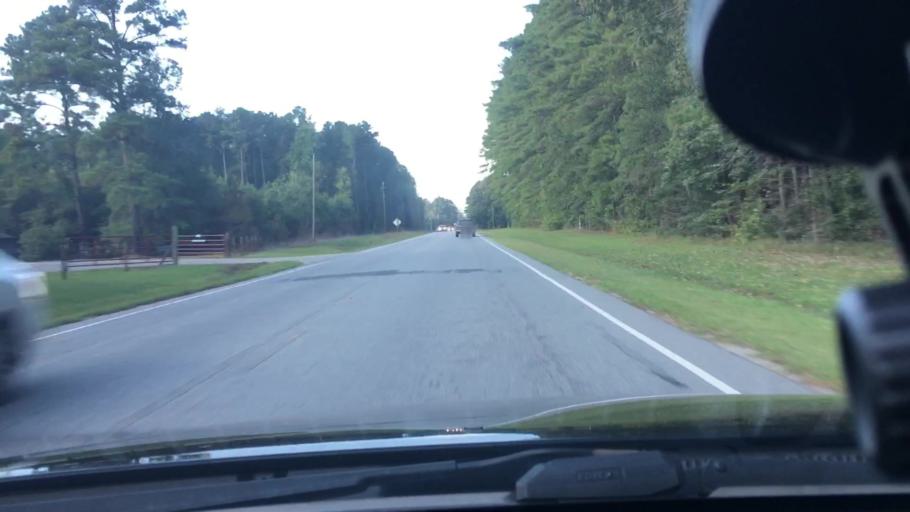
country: US
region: North Carolina
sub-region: Pitt County
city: Windsor
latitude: 35.4403
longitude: -77.2632
